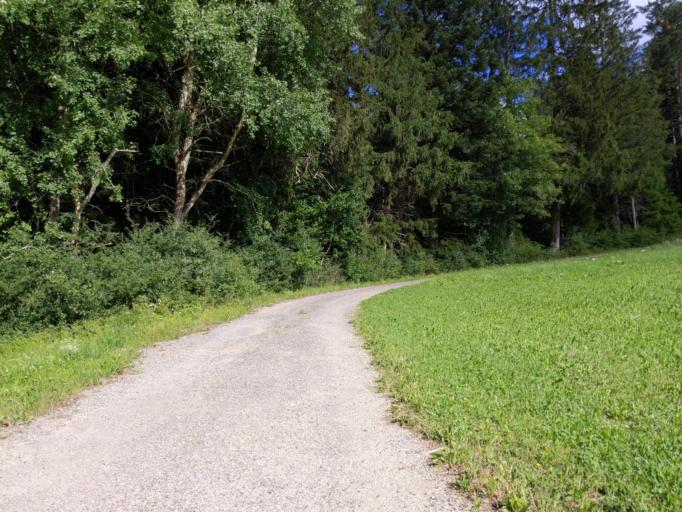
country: DE
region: Baden-Wuerttemberg
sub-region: Karlsruhe Region
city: Glatten
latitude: 48.4008
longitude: 8.5051
